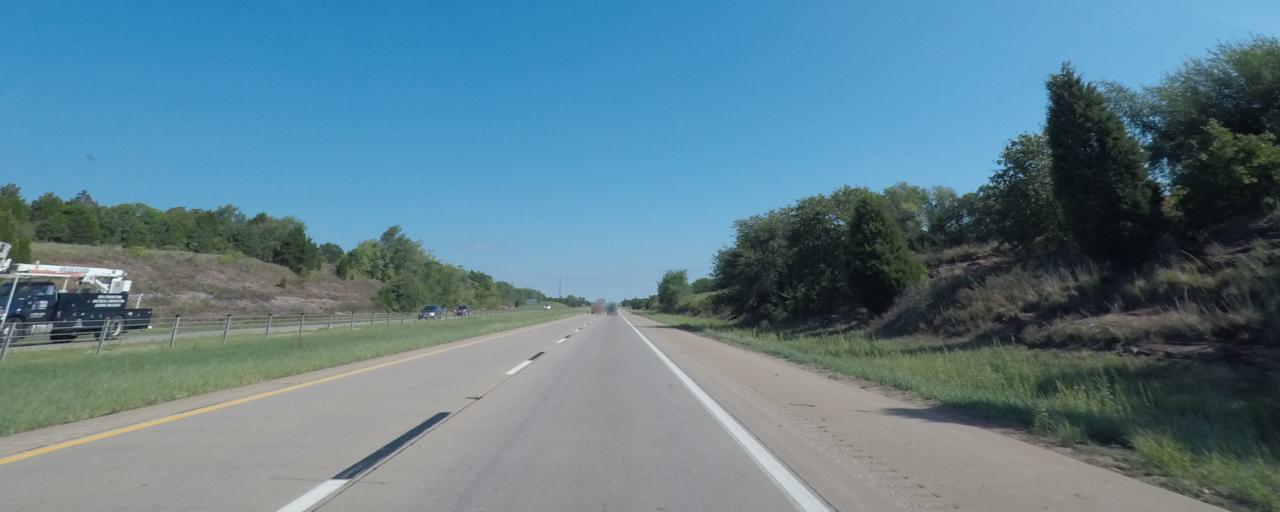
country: US
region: Oklahoma
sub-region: Oklahoma County
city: Edmond
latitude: 35.7408
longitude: -97.4162
